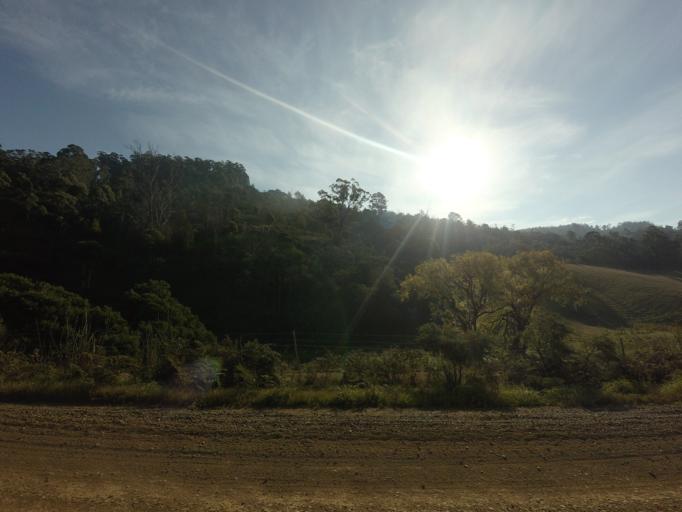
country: AU
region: Tasmania
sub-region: Brighton
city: Bridgewater
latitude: -42.5063
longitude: 147.4288
